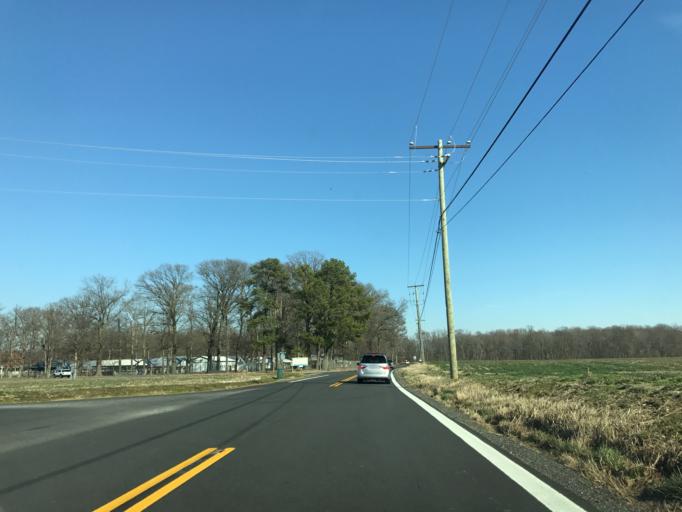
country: US
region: Maryland
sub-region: Queen Anne's County
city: Centreville
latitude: 39.0273
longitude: -76.1208
